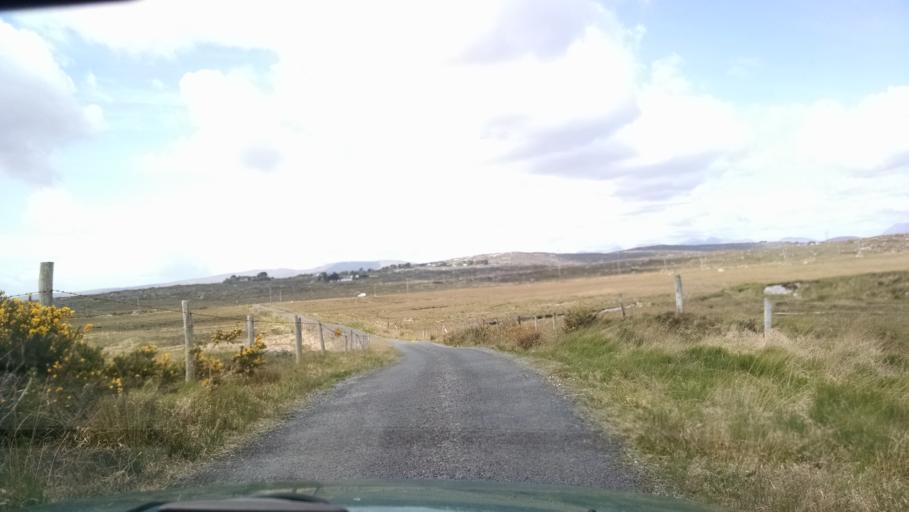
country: IE
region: Connaught
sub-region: County Galway
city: Oughterard
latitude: 53.3467
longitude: -9.5377
